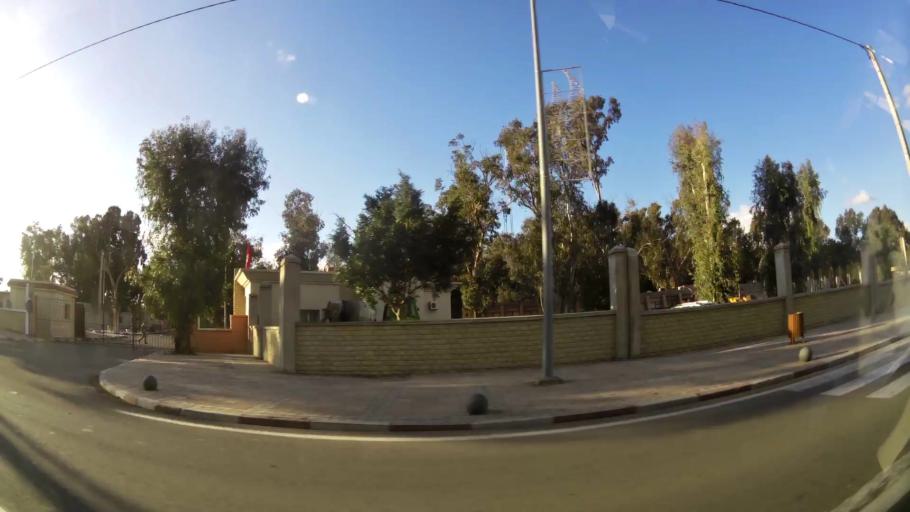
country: MA
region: Marrakech-Tensift-Al Haouz
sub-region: Kelaa-Des-Sraghna
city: Sidi Bou Othmane
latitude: 32.2290
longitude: -7.9593
